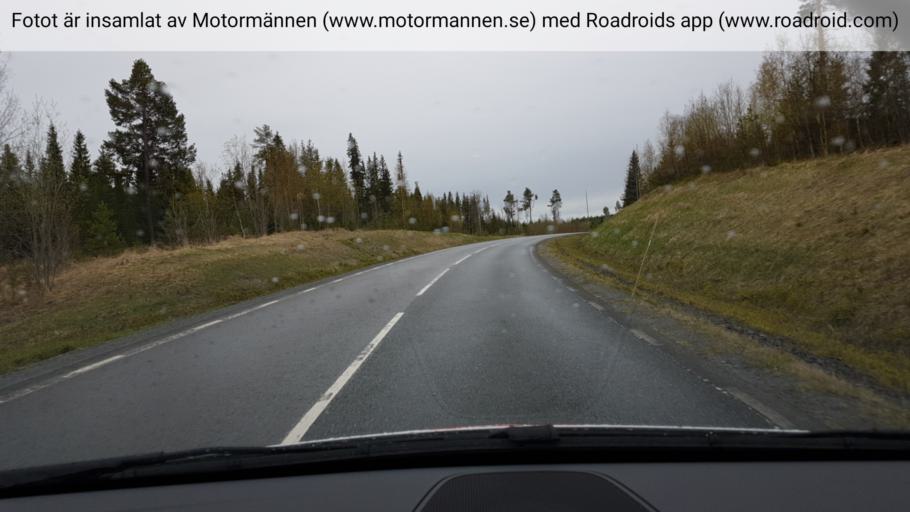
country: SE
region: Jaemtland
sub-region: Krokoms Kommun
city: Krokom
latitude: 63.2698
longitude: 14.4376
